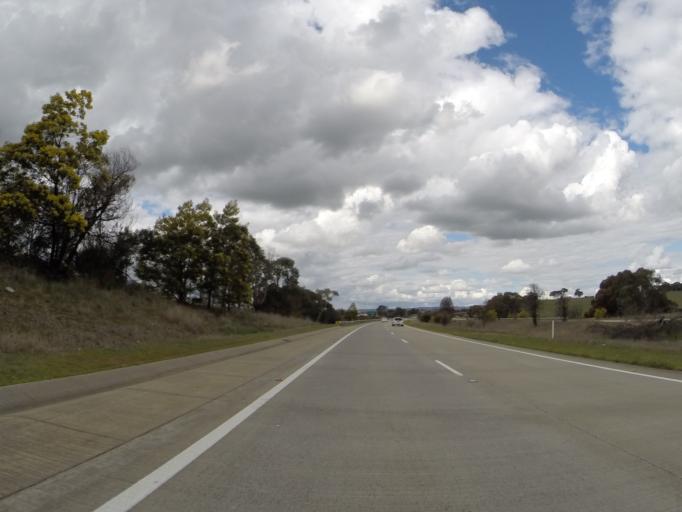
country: AU
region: New South Wales
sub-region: Yass Valley
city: Gundaroo
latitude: -34.7850
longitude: 149.2477
